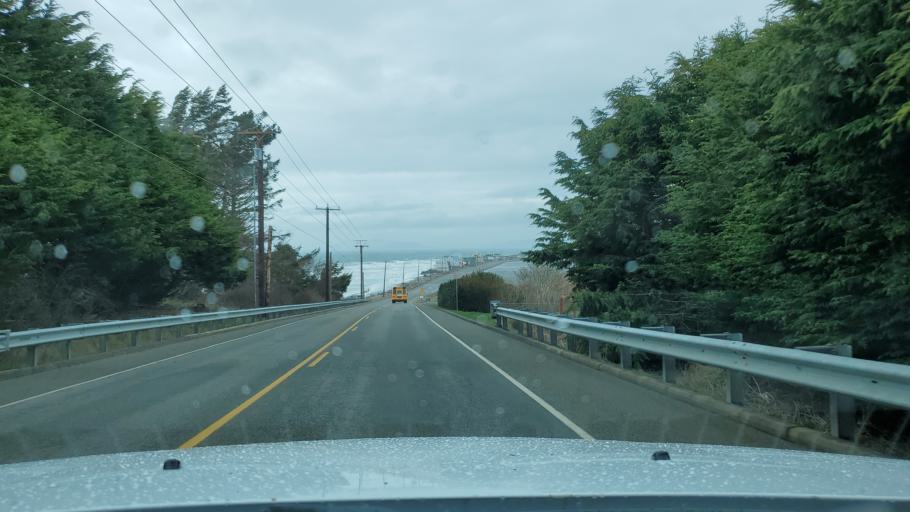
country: US
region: Washington
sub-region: Island County
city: Ault Field
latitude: 48.2961
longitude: -122.7251
